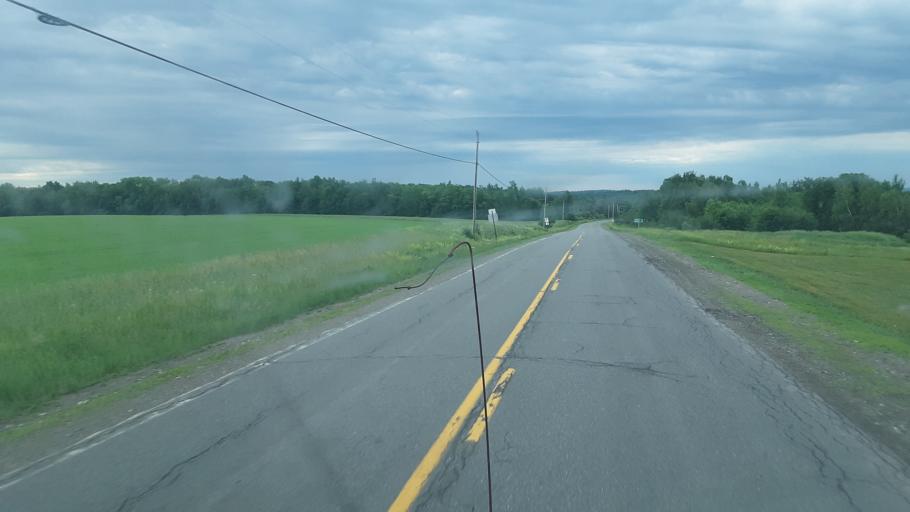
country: US
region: Maine
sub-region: Penobscot County
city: Patten
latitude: 45.8692
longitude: -68.3299
